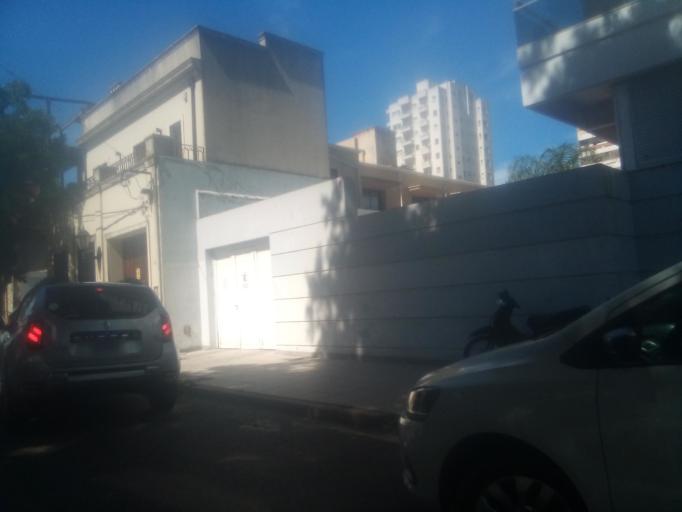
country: AR
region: Corrientes
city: Corrientes
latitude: -27.4646
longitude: -58.8429
